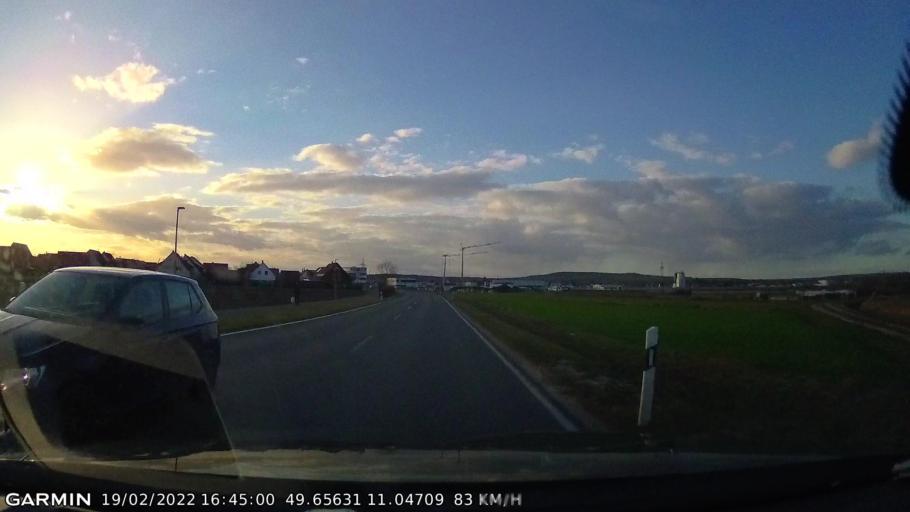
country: DE
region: Bavaria
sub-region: Regierungsbezirk Mittelfranken
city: Baiersdorf
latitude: 49.6575
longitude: 11.0462
